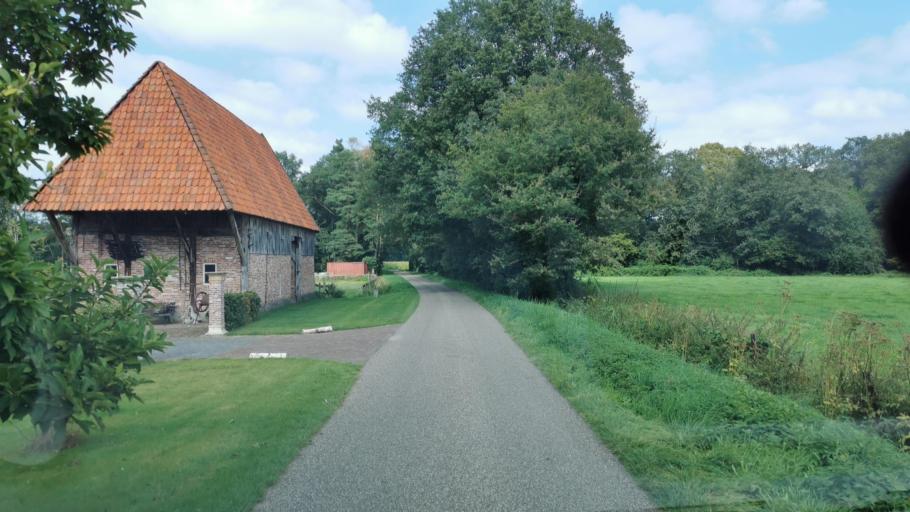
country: NL
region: Overijssel
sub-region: Gemeente Oldenzaal
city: Oldenzaal
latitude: 52.3411
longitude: 6.9047
